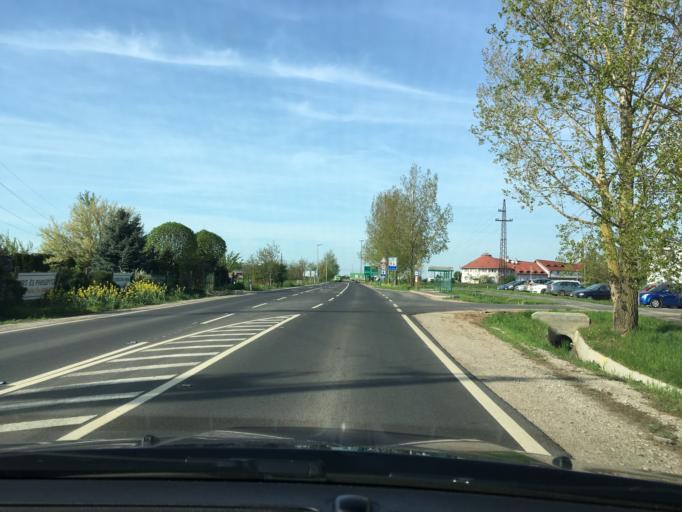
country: HU
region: Bekes
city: Bekescsaba
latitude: 46.6827
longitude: 21.0488
